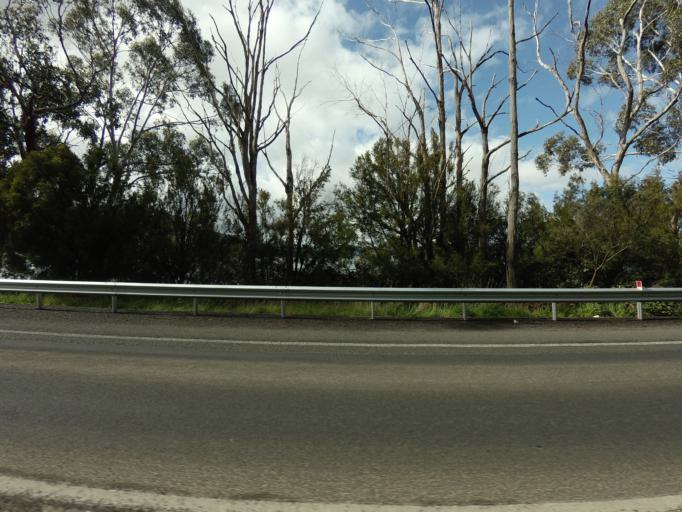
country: AU
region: Tasmania
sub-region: Huon Valley
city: Geeveston
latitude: -43.1441
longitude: 146.9764
